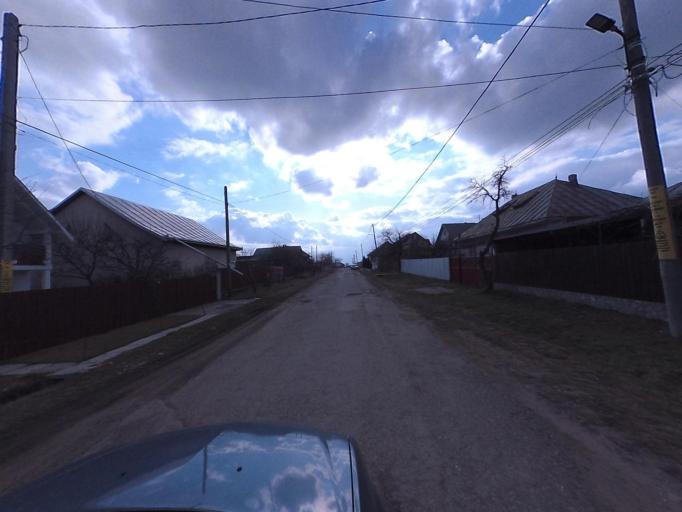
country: RO
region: Neamt
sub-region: Oras Targu Neamt
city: Targu Neamt
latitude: 47.2135
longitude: 26.3797
